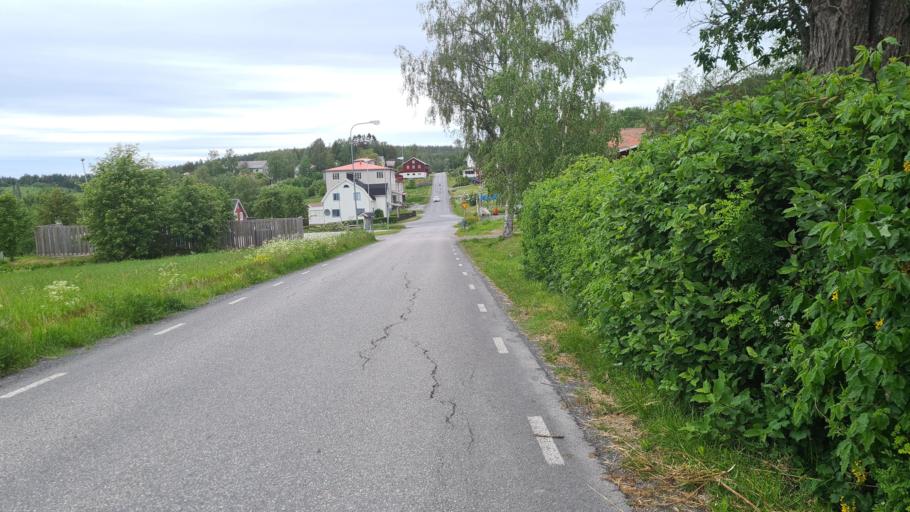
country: SE
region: Vaesternorrland
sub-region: Kramfors Kommun
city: Nordingra
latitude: 62.9850
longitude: 18.4319
